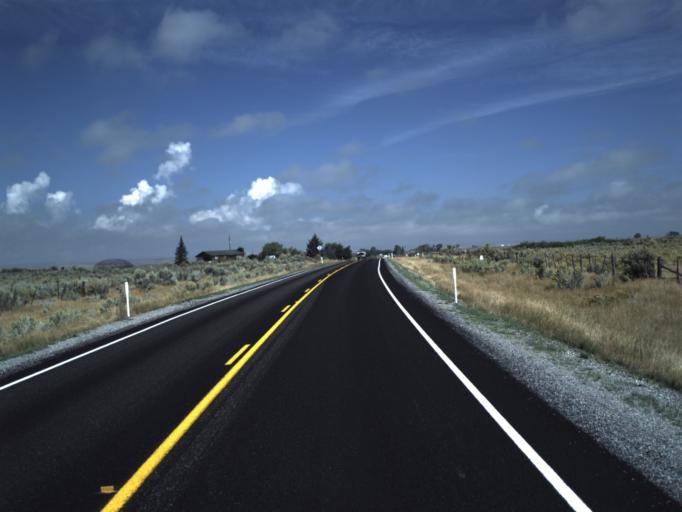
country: US
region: Utah
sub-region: Rich County
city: Randolph
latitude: 41.6117
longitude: -111.1791
